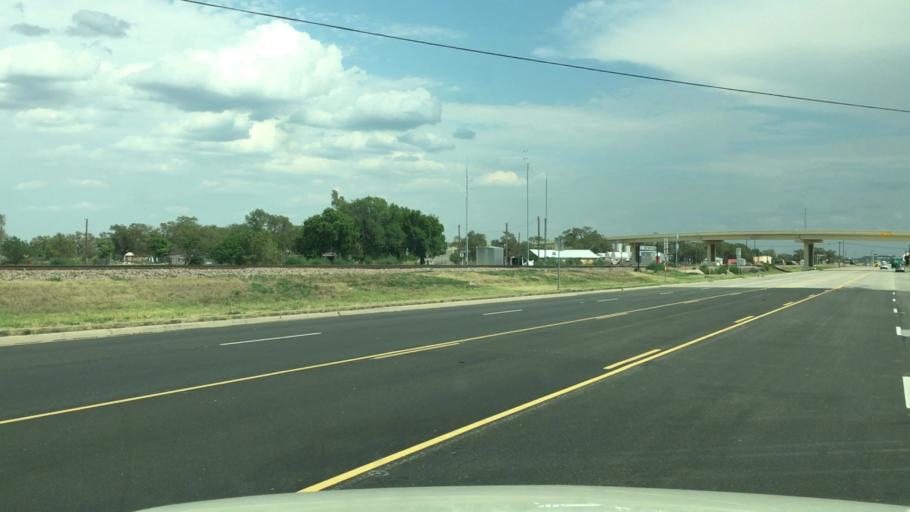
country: US
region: Texas
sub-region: Hall County
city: Memphis
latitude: 34.7291
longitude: -100.5385
